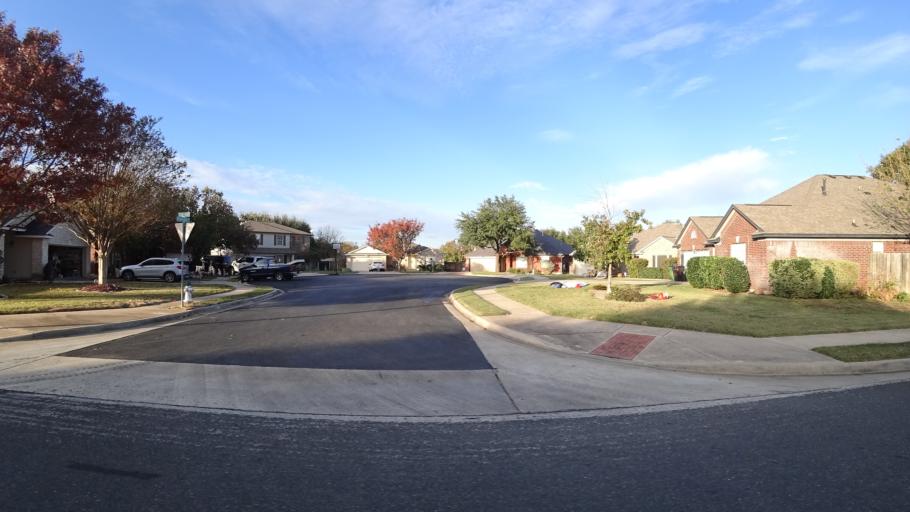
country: US
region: Texas
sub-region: Williamson County
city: Brushy Creek
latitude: 30.4977
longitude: -97.7282
